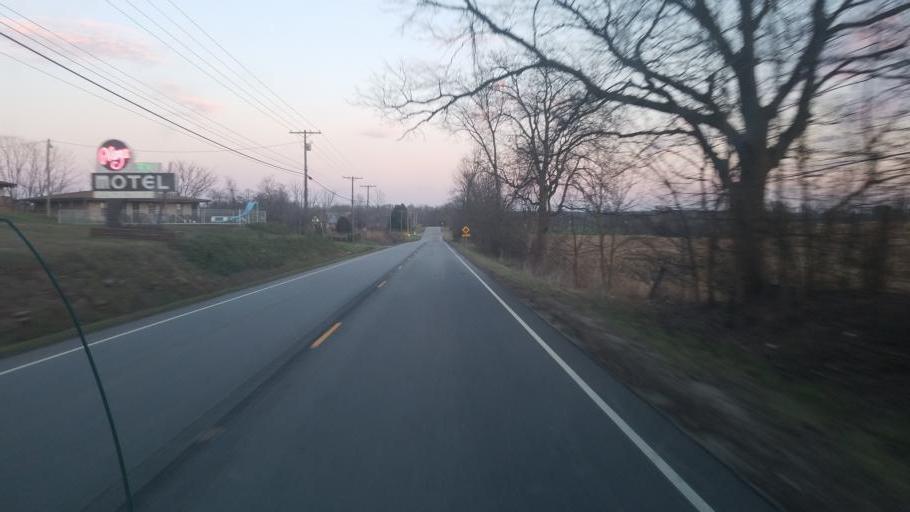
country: US
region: Indiana
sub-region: Lawrence County
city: Bedford
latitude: 38.8744
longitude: -86.3266
